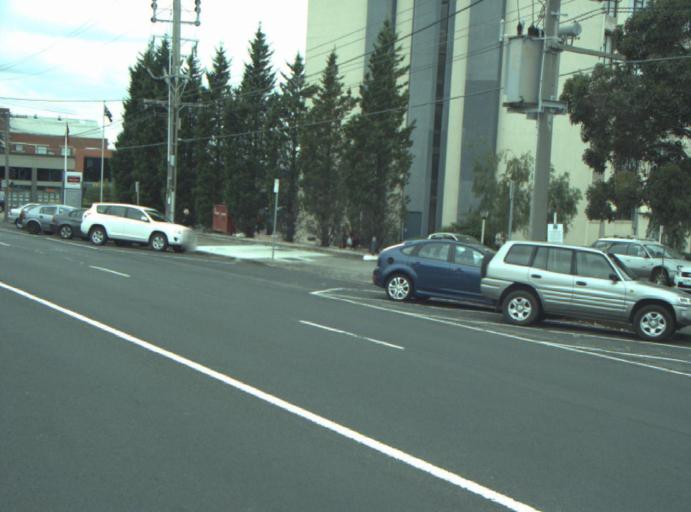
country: AU
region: Victoria
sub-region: Greater Geelong
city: Geelong
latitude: -38.1515
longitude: 144.3559
